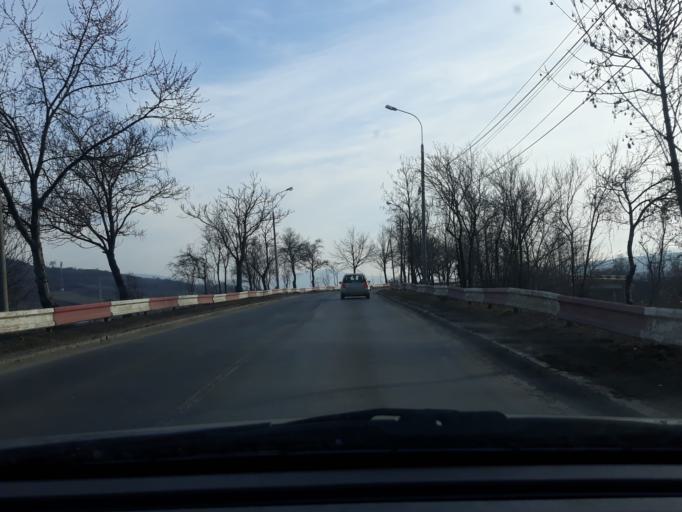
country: RO
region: Salaj
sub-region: Comuna Criseni
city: Criseni
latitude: 47.2189
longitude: 23.0425
